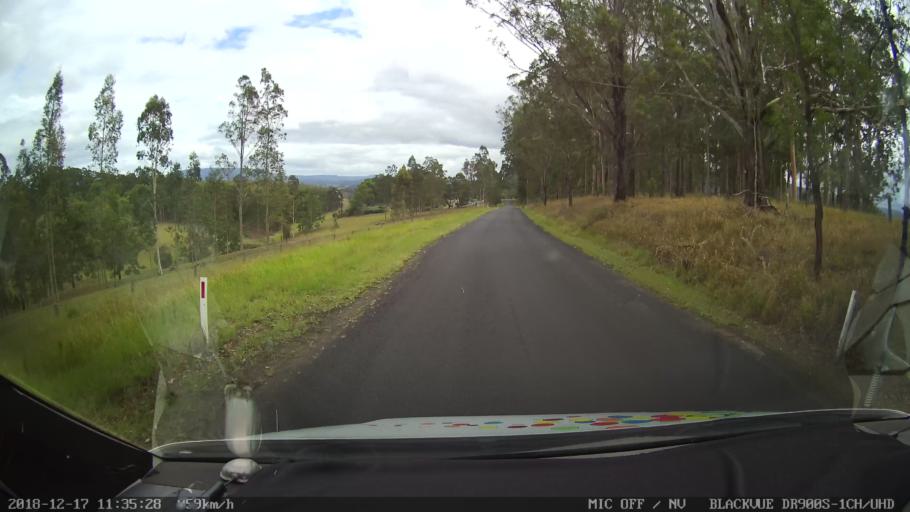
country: AU
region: New South Wales
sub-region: Kyogle
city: Kyogle
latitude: -28.7225
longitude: 152.6065
